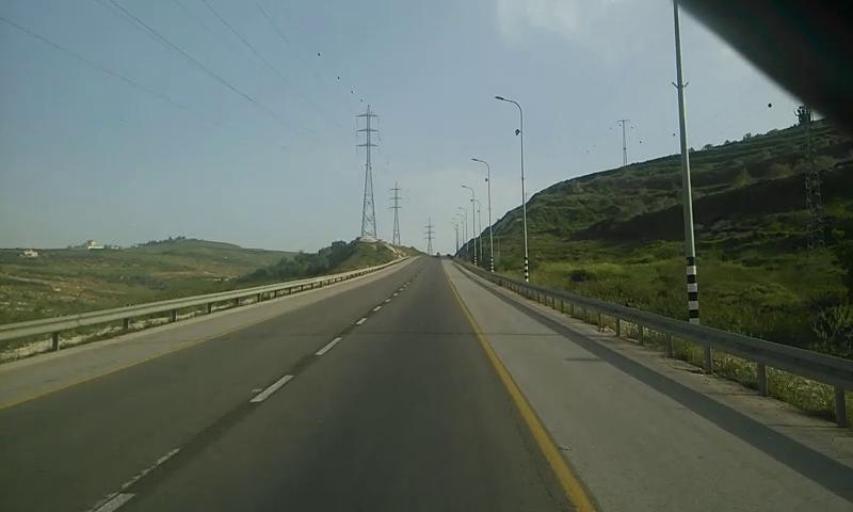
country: PS
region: West Bank
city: Sarrah
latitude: 32.2096
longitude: 35.1819
